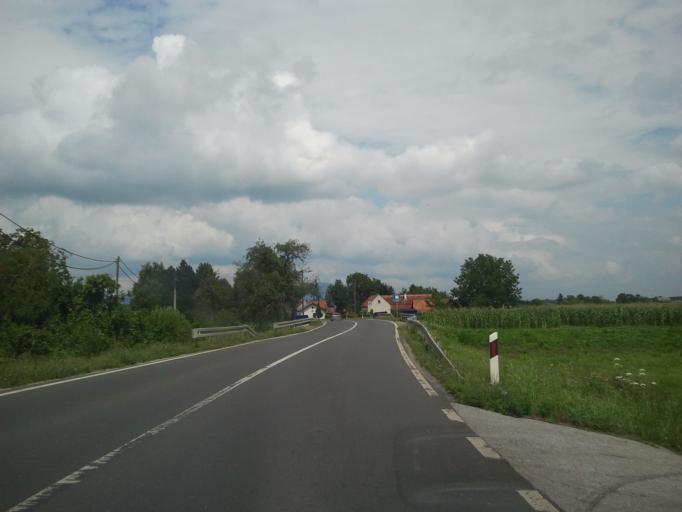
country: HR
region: Zagrebacka
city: Jastrebarsko
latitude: 45.6163
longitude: 15.5972
